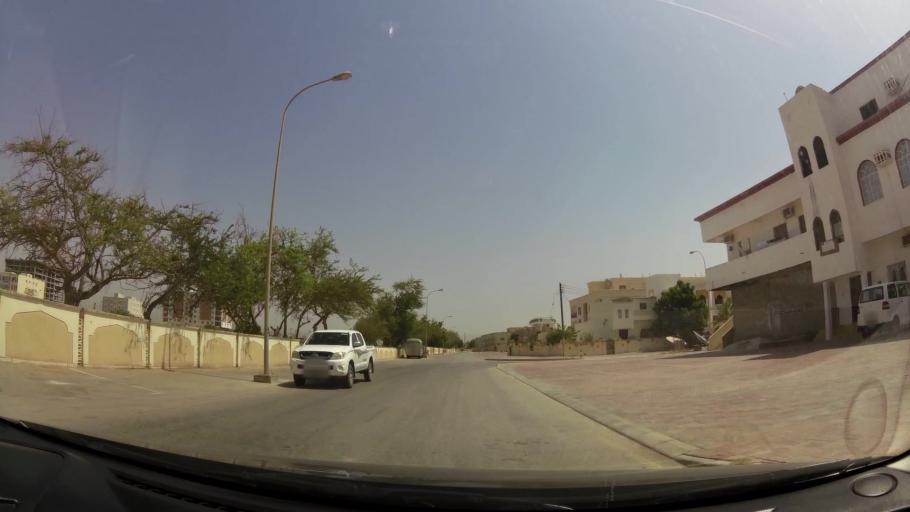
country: OM
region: Zufar
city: Salalah
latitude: 17.0203
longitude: 54.1041
